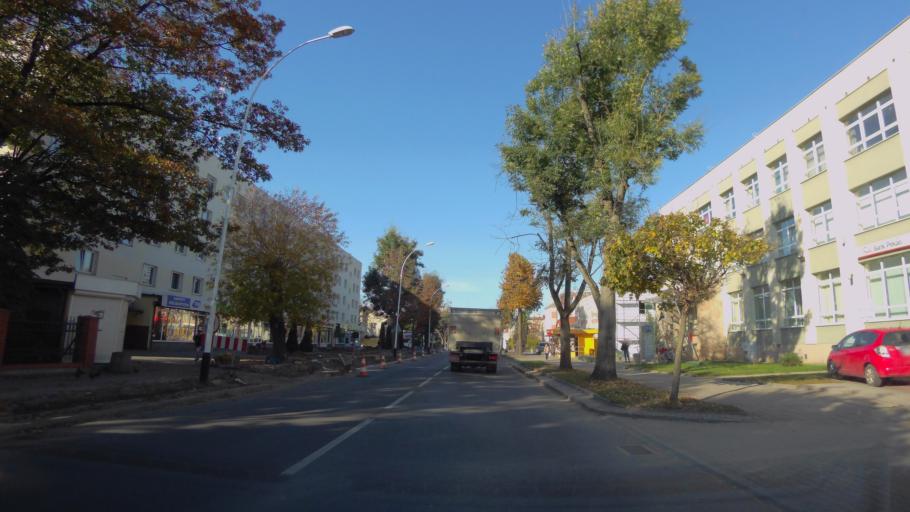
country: PL
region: Subcarpathian Voivodeship
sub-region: Powiat lezajski
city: Lezajsk
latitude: 50.2595
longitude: 22.4203
